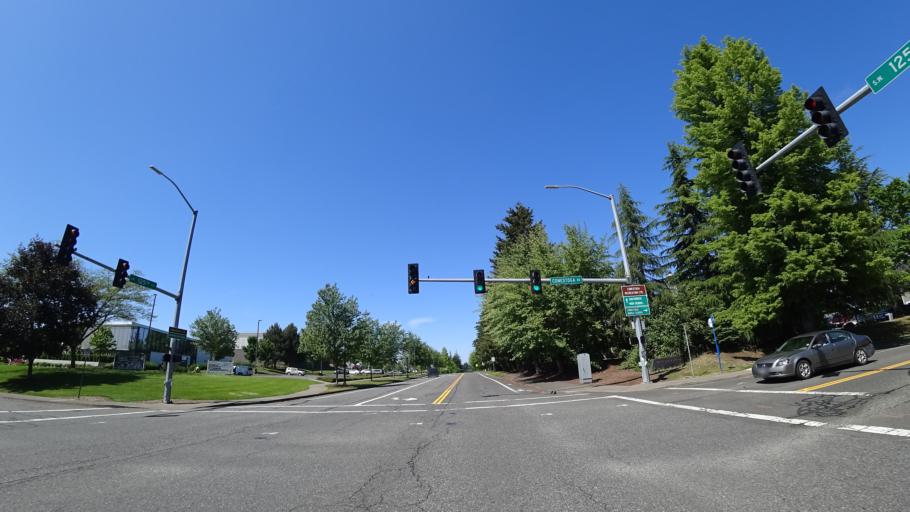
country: US
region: Oregon
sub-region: Washington County
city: Tigard
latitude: 45.4474
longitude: -122.8054
